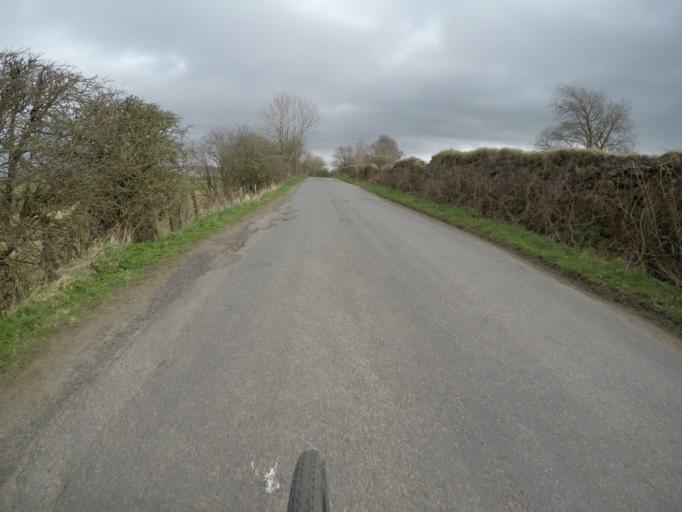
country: GB
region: Scotland
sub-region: East Ayrshire
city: Stewarton
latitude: 55.6789
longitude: -4.5355
